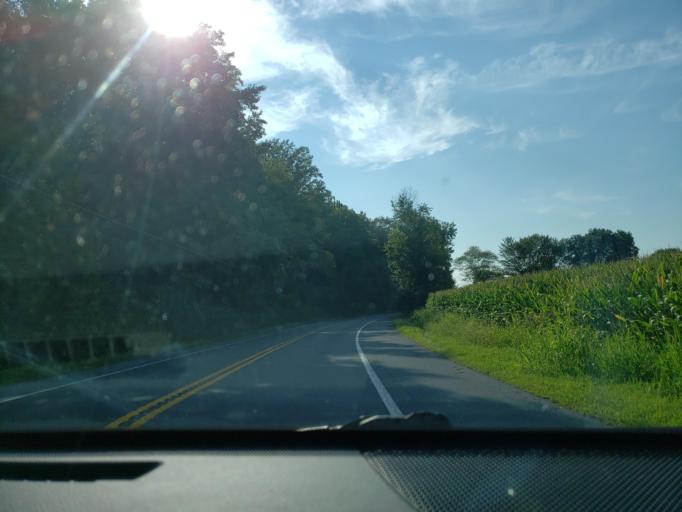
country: US
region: Delaware
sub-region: Sussex County
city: Milton
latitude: 38.7548
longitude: -75.2544
